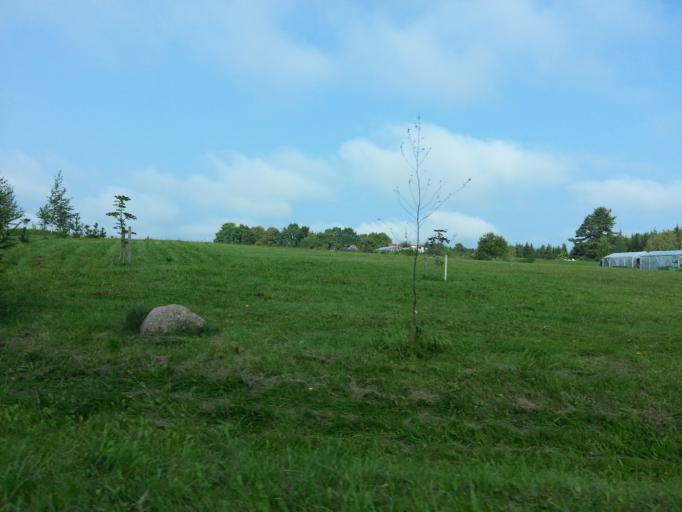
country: LT
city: Grigiskes
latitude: 54.7695
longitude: 25.0527
